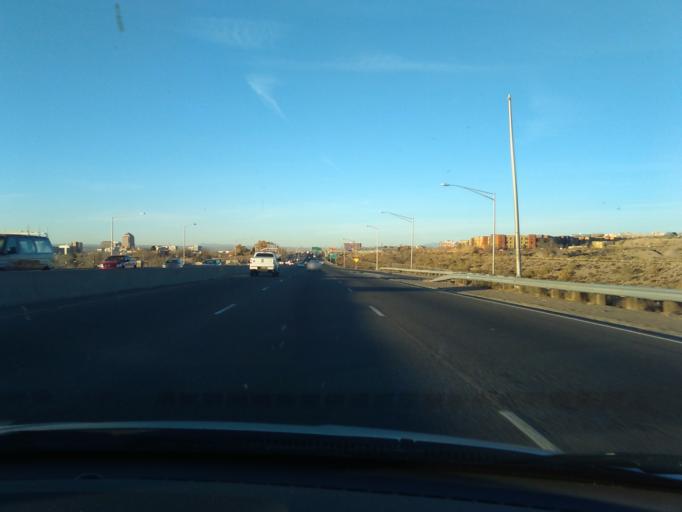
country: US
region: New Mexico
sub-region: Bernalillo County
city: Albuquerque
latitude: 35.0610
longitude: -106.6383
